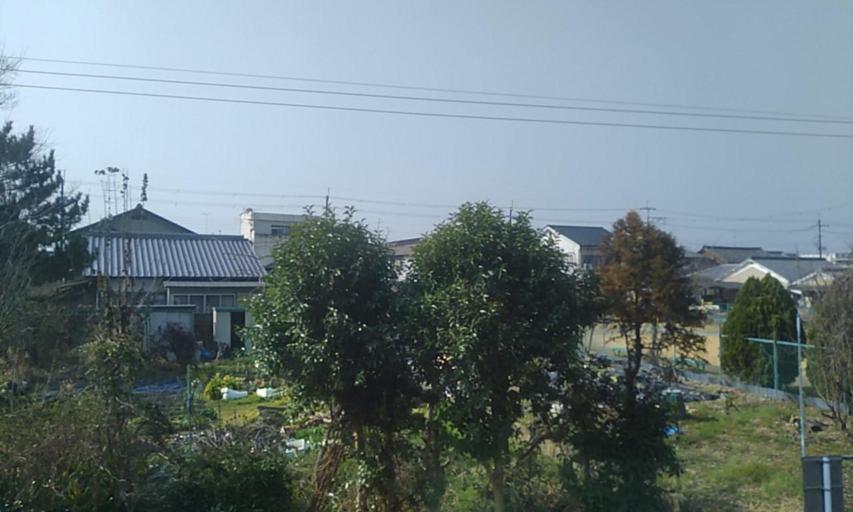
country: JP
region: Kyoto
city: Tanabe
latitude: 34.8417
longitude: 135.7913
